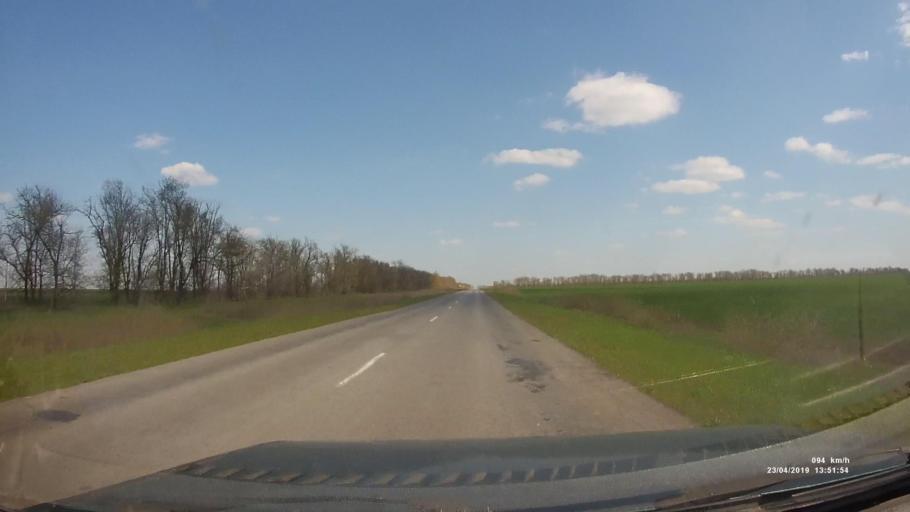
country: RU
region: Rostov
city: Remontnoye
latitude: 46.5997
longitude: 42.9428
